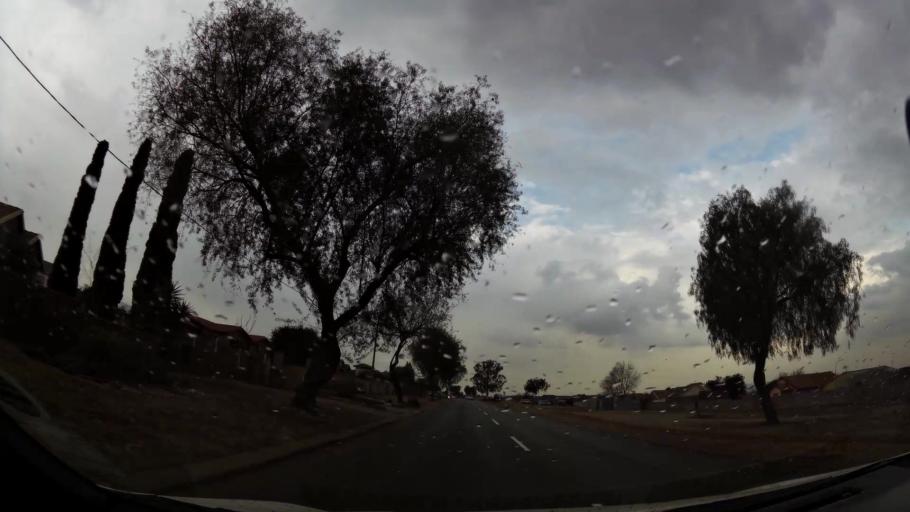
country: ZA
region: Gauteng
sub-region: Ekurhuleni Metropolitan Municipality
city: Germiston
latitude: -26.3813
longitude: 28.1239
